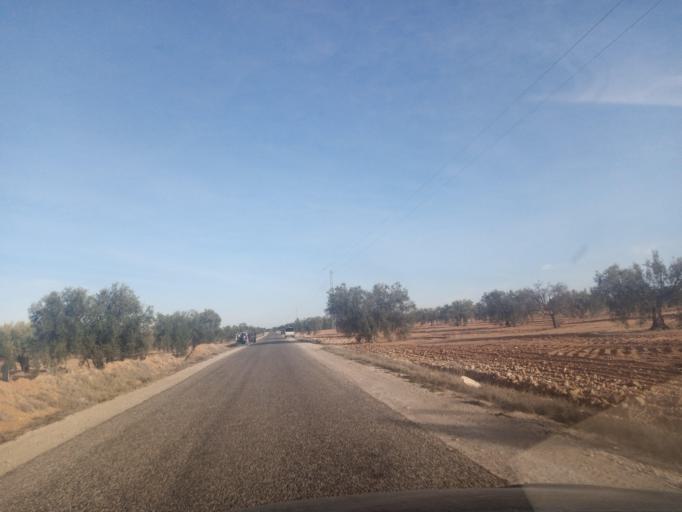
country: TN
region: Safaqis
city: Bi'r `Ali Bin Khalifah
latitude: 34.8875
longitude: 10.1830
